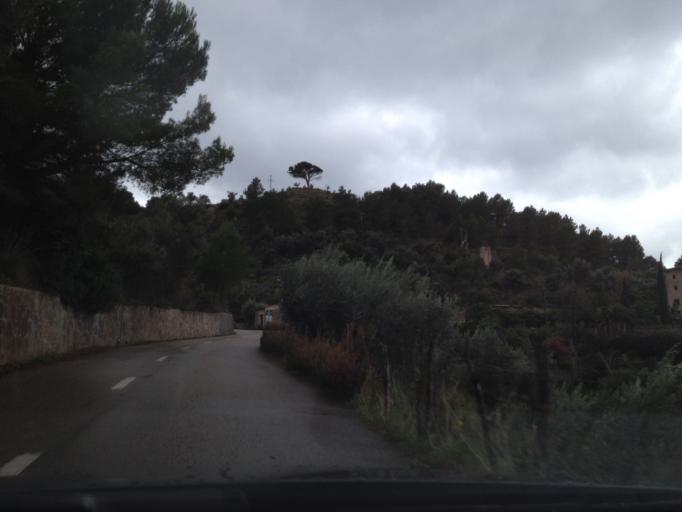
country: ES
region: Balearic Islands
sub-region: Illes Balears
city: Soller
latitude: 39.7727
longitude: 2.6785
